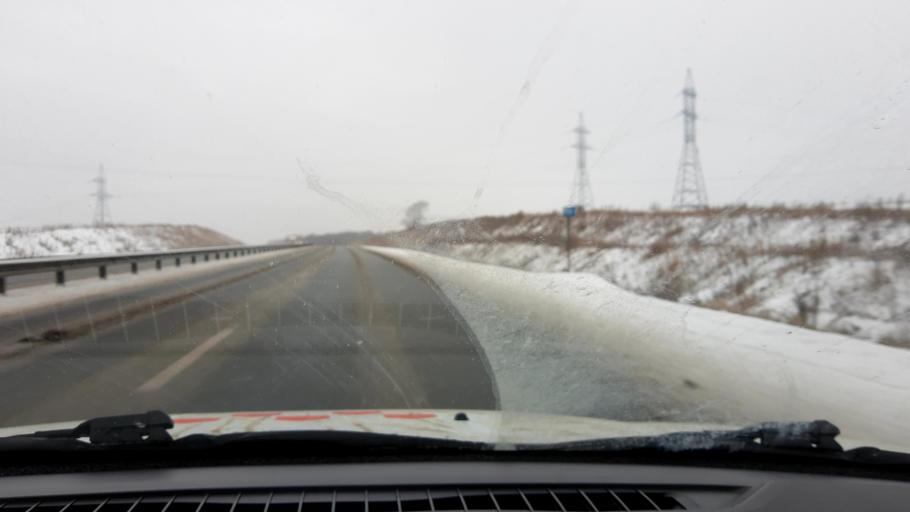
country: RU
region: Nizjnij Novgorod
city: Kstovo
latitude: 56.0998
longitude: 44.0551
